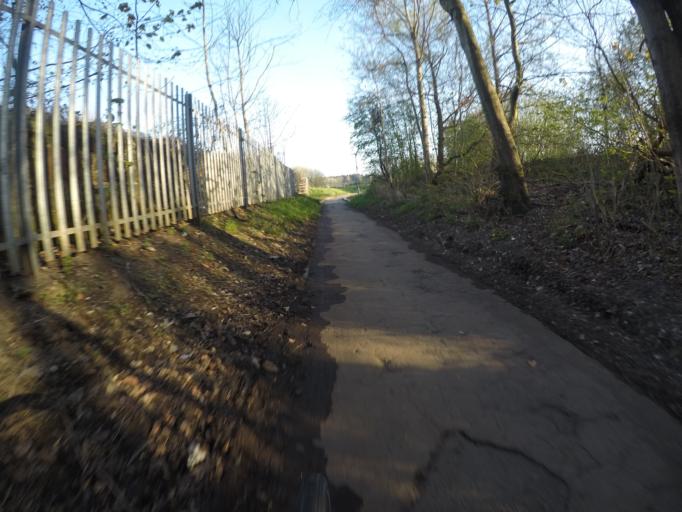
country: GB
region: Scotland
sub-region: North Ayrshire
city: Kilwinning
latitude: 55.6506
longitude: -4.7071
